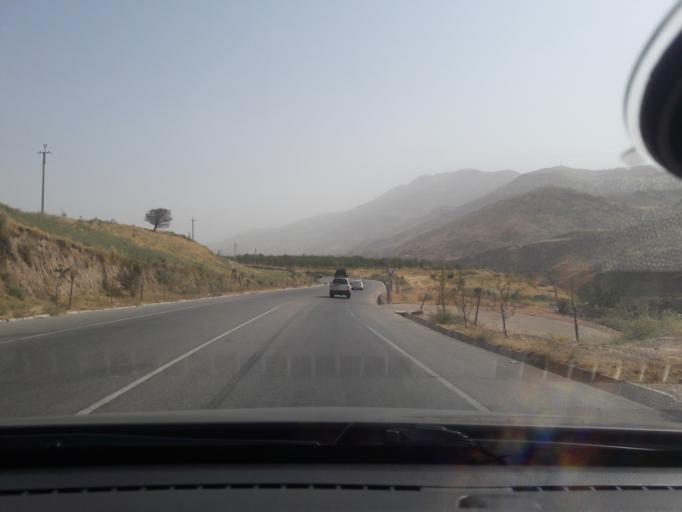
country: TJ
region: Republican Subordination
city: Vahdat
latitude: 38.4879
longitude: 69.1670
